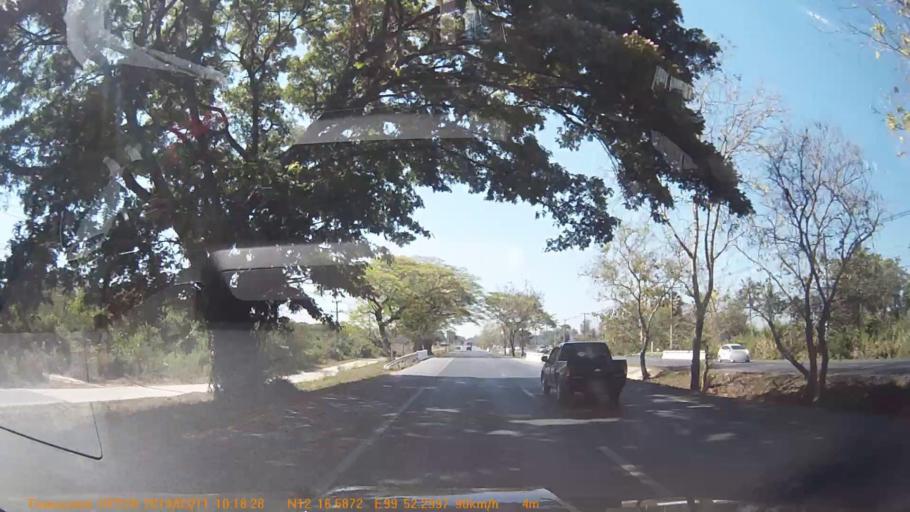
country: TH
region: Prachuap Khiri Khan
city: Sam Roi Yot
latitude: 12.2760
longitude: 99.8716
